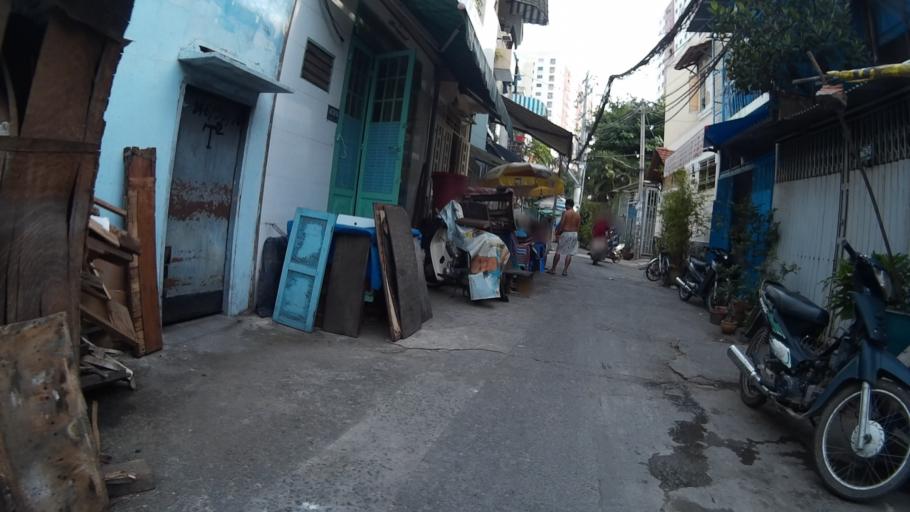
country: VN
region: Ho Chi Minh City
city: Quan Binh Thanh
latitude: 10.8007
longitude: 106.7020
